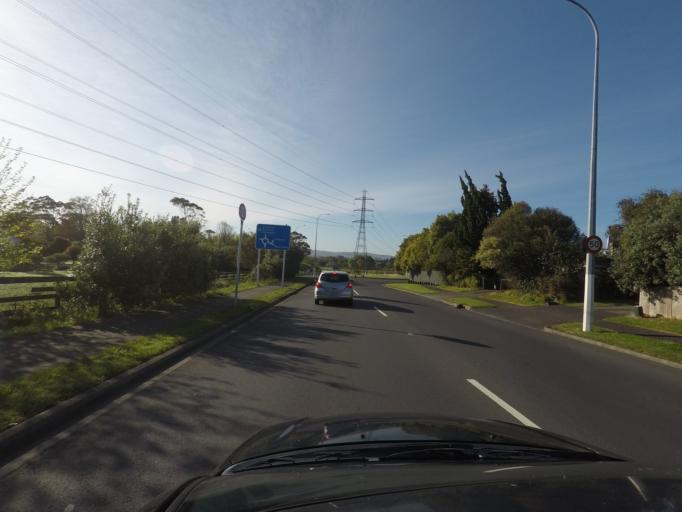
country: NZ
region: Auckland
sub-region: Auckland
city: Takanini
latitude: -37.0151
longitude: 174.9205
